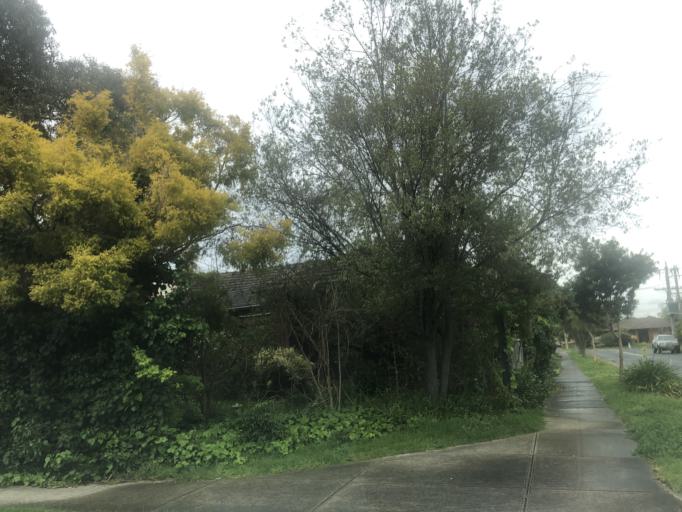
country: AU
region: Victoria
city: Burwood East
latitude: -37.8576
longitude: 145.1523
